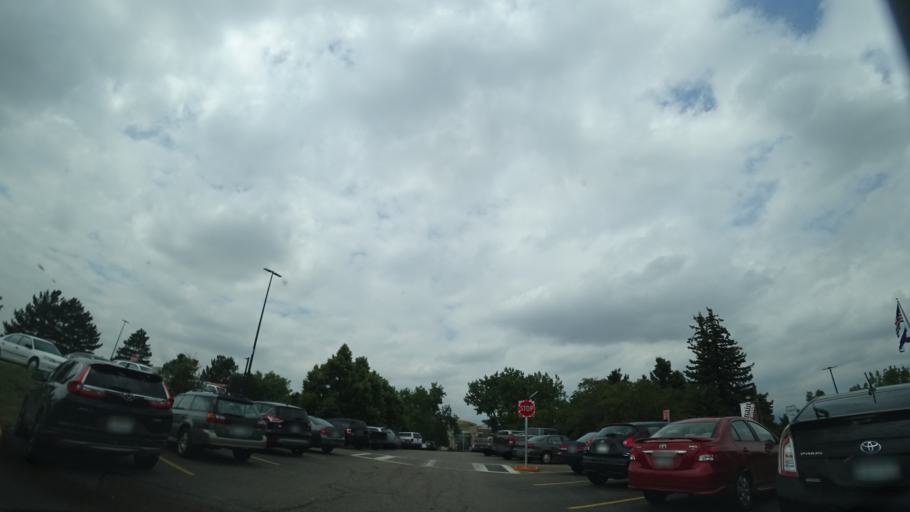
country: US
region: Colorado
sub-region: Jefferson County
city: West Pleasant View
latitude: 39.7189
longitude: -105.1495
